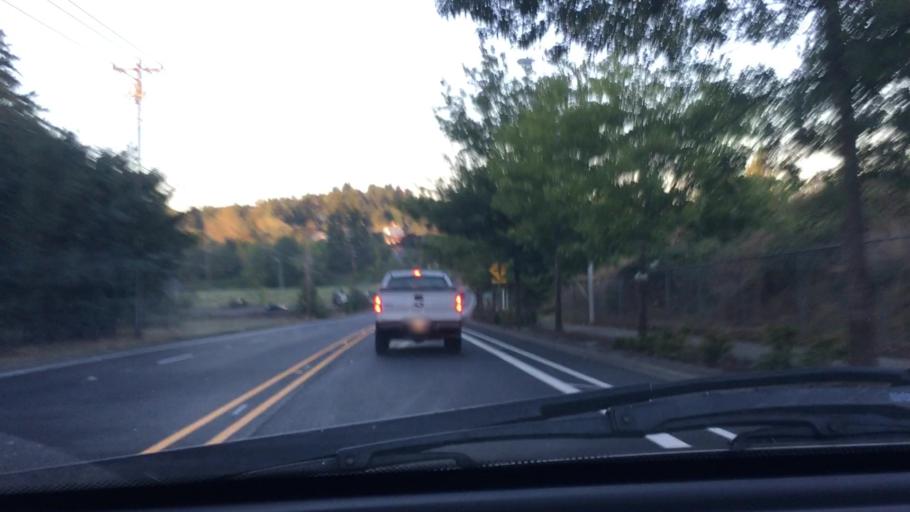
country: US
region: Oregon
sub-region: Washington County
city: Sherwood
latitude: 45.3625
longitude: -122.8223
